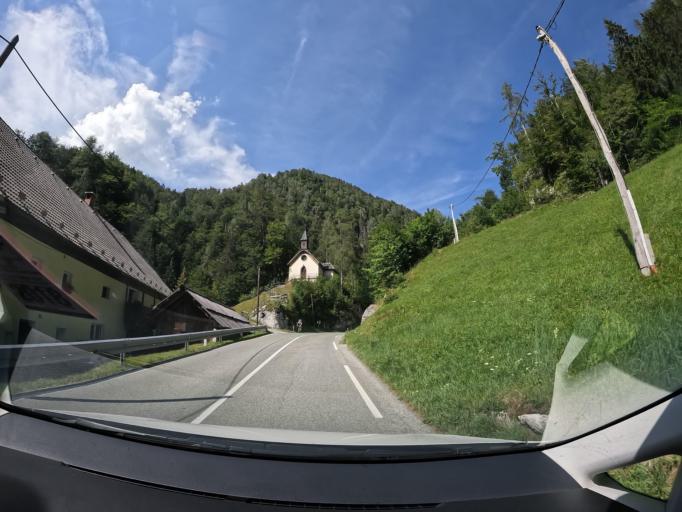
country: SI
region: Trzic
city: Trzic
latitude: 46.4121
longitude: 14.2988
